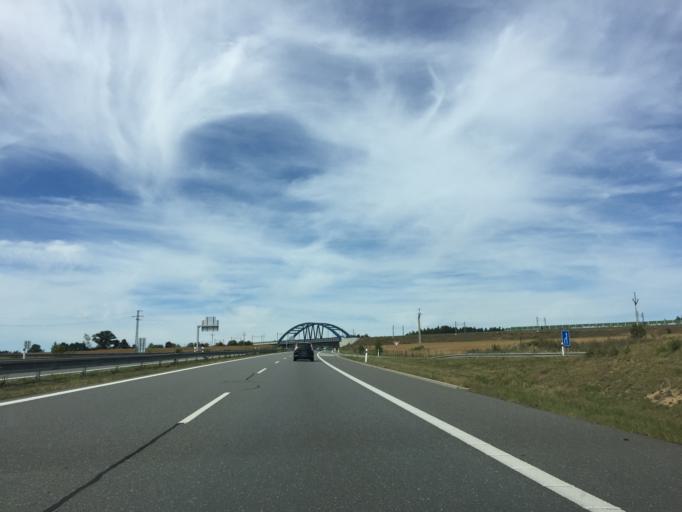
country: CZ
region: Jihocesky
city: Chotoviny
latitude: 49.4746
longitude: 14.6601
